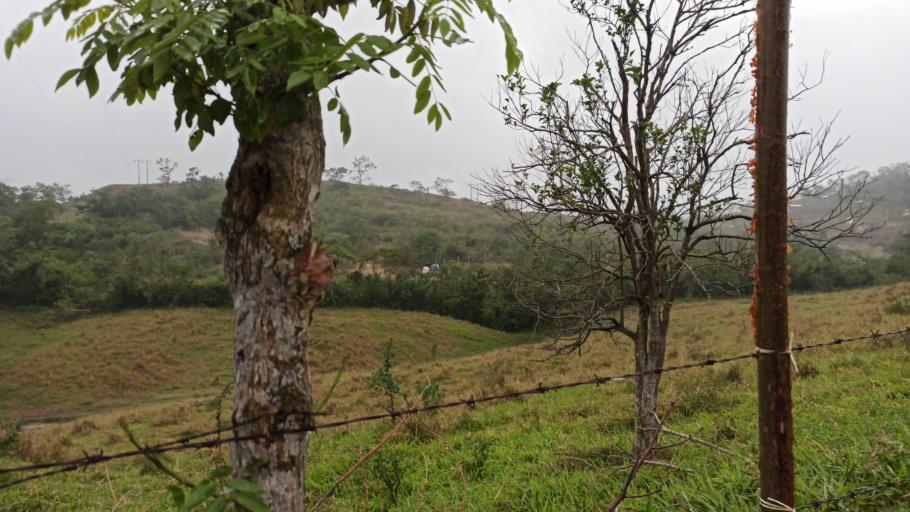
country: MX
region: Veracruz
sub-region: Papantla
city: El Chote
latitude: 20.3933
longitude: -97.3261
